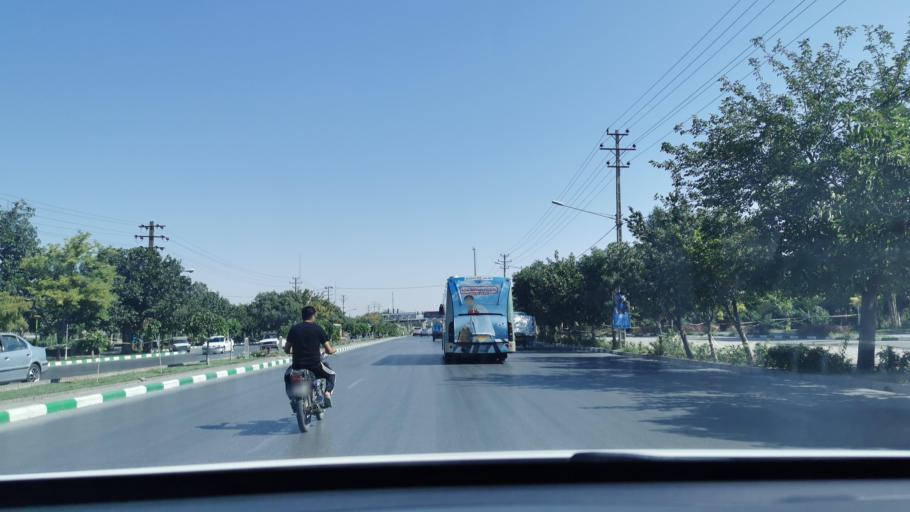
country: IR
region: Razavi Khorasan
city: Mashhad
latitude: 36.3330
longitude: 59.6253
